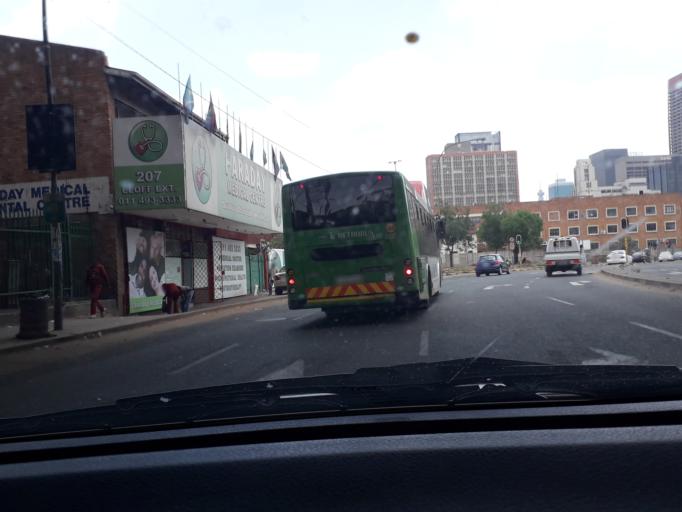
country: ZA
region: Gauteng
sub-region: City of Johannesburg Metropolitan Municipality
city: Johannesburg
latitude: -26.2129
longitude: 28.0436
